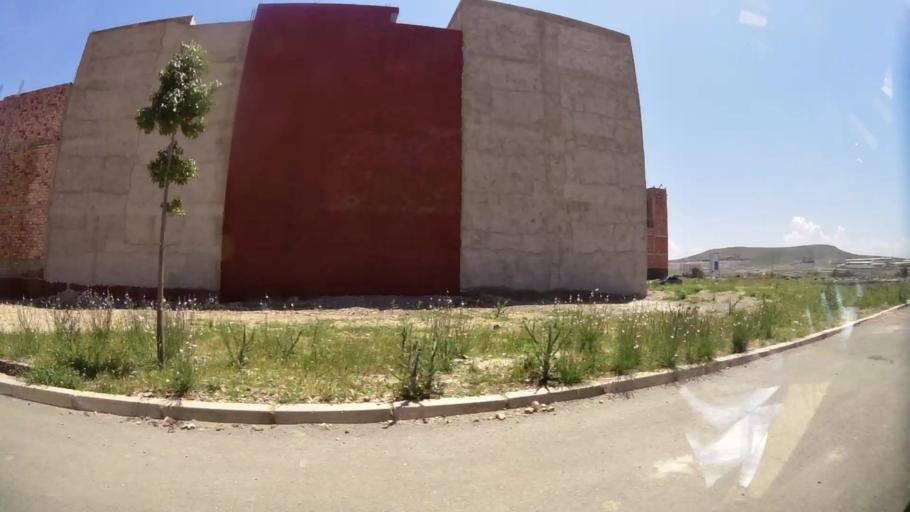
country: MA
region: Oriental
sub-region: Oujda-Angad
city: Oujda
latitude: 34.6585
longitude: -1.9543
